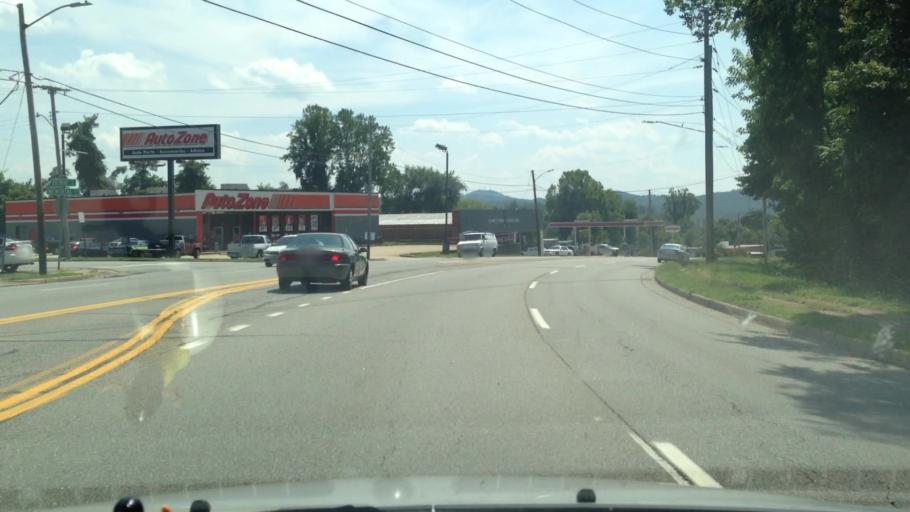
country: US
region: Virginia
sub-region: City of Martinsville
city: Martinsville
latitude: 36.6724
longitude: -79.8787
